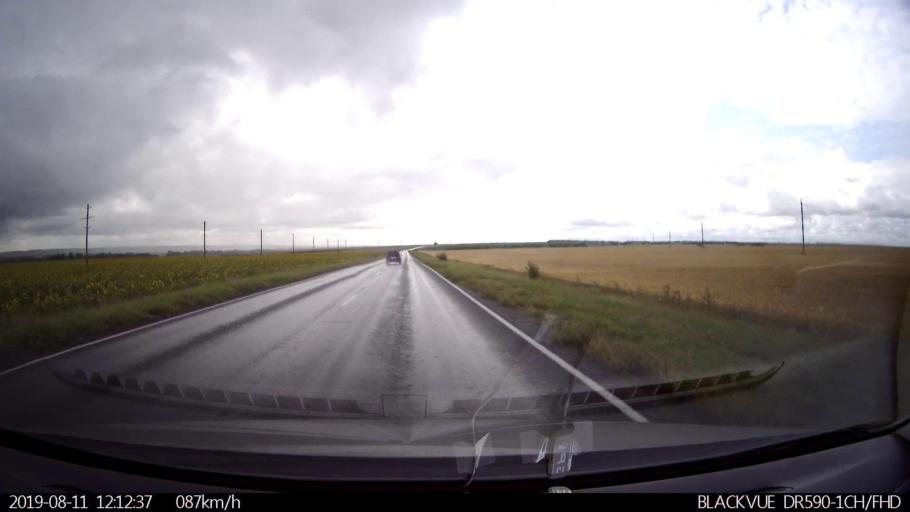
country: RU
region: Ulyanovsk
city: Silikatnyy
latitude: 53.9708
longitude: 47.9958
